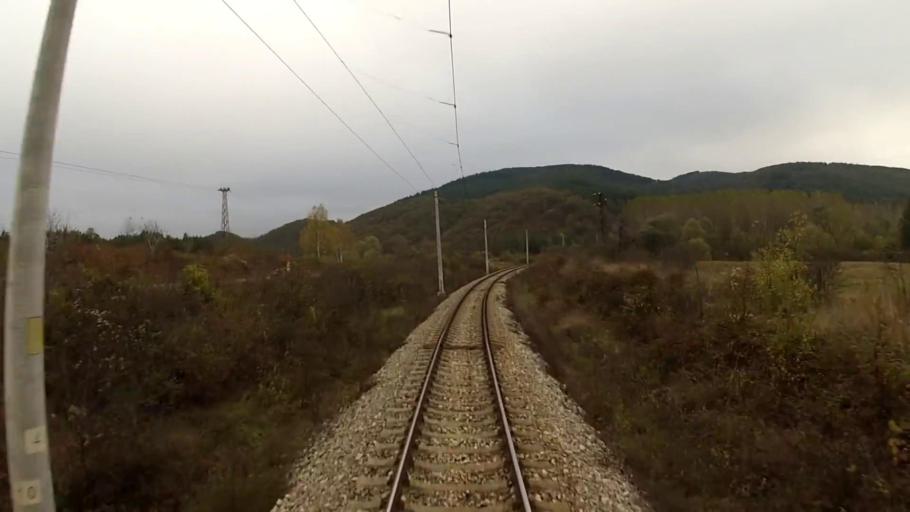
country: BG
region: Sofiya
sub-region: Obshtina Dragoman
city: Dragoman
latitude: 42.9561
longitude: 22.9055
